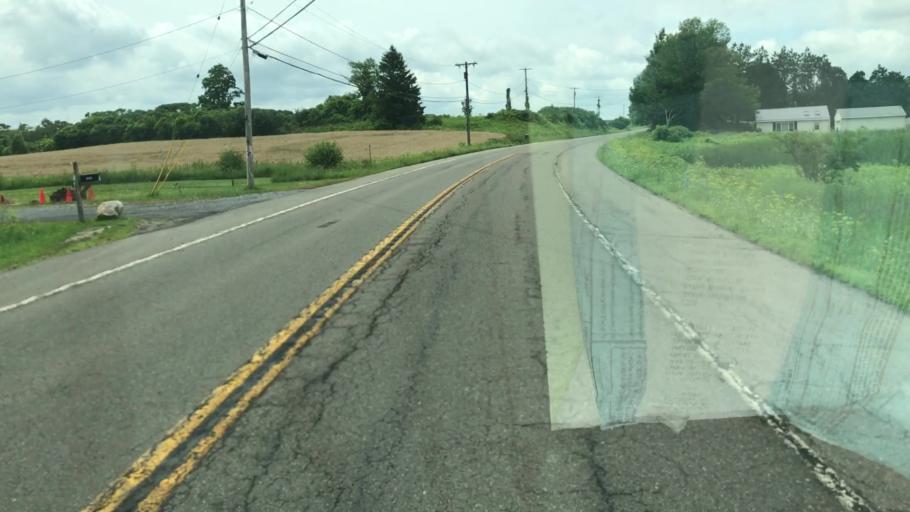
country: US
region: New York
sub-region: Onondaga County
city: Manlius
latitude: 42.8941
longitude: -76.0365
